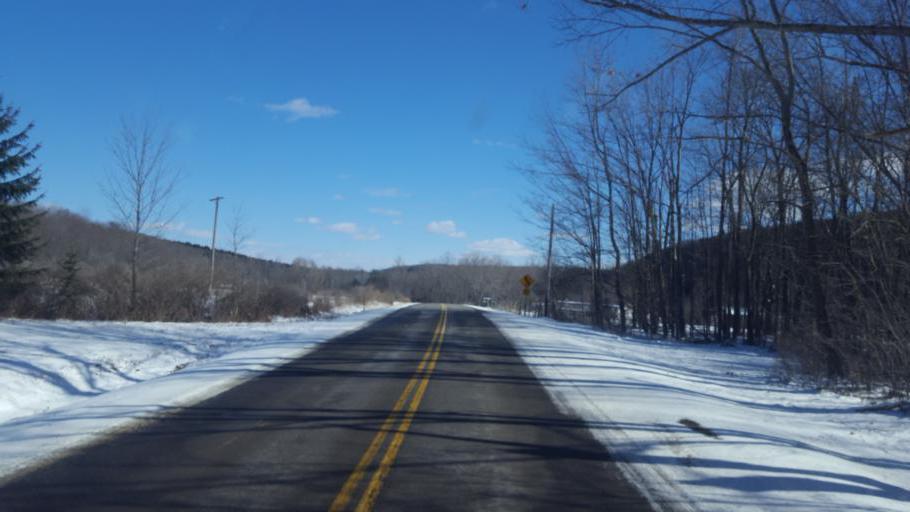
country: US
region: New York
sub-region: Allegany County
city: Belmont
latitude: 42.1744
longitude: -78.0683
